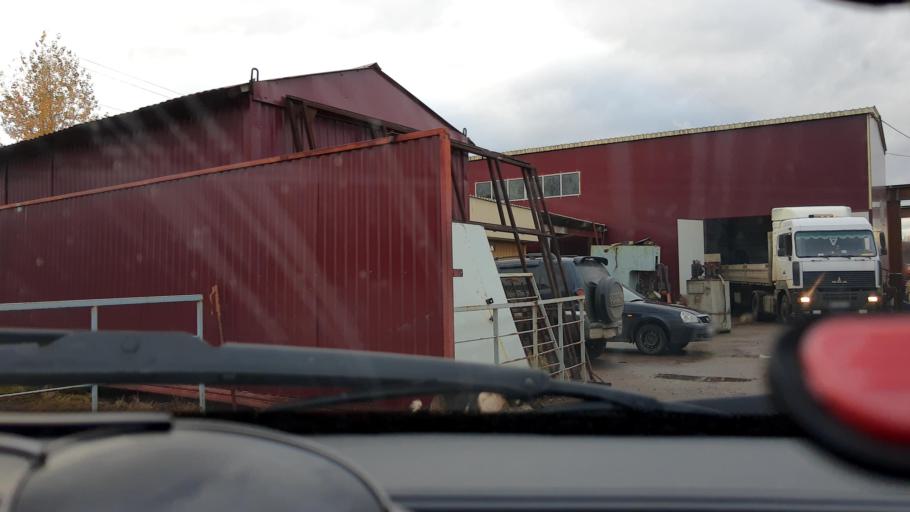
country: RU
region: Bashkortostan
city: Ufa
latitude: 54.8367
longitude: 56.1122
